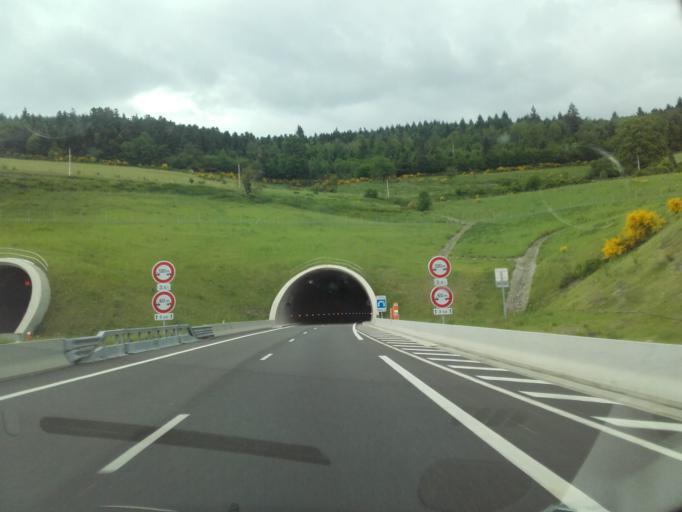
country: FR
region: Rhone-Alpes
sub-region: Departement du Rhone
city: Tarare
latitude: 45.8878
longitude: 4.4171
